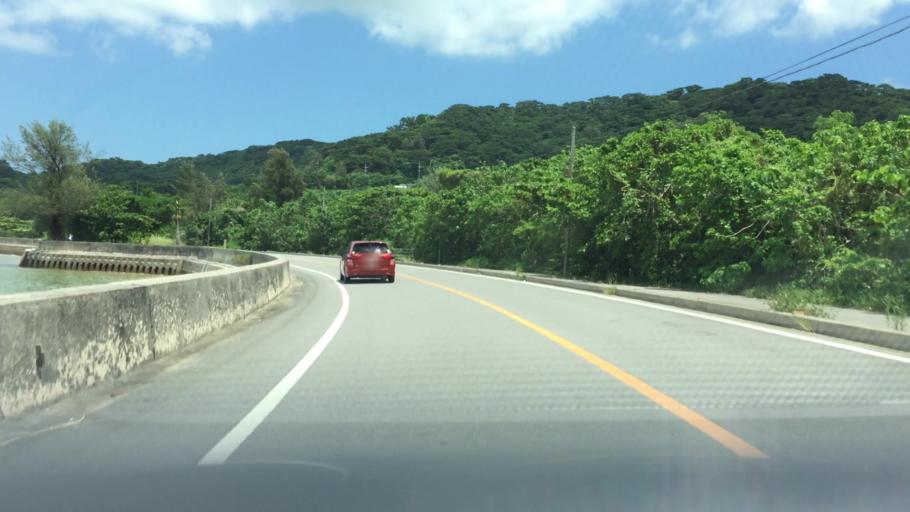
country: JP
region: Okinawa
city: Ishigaki
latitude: 24.4303
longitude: 124.1250
